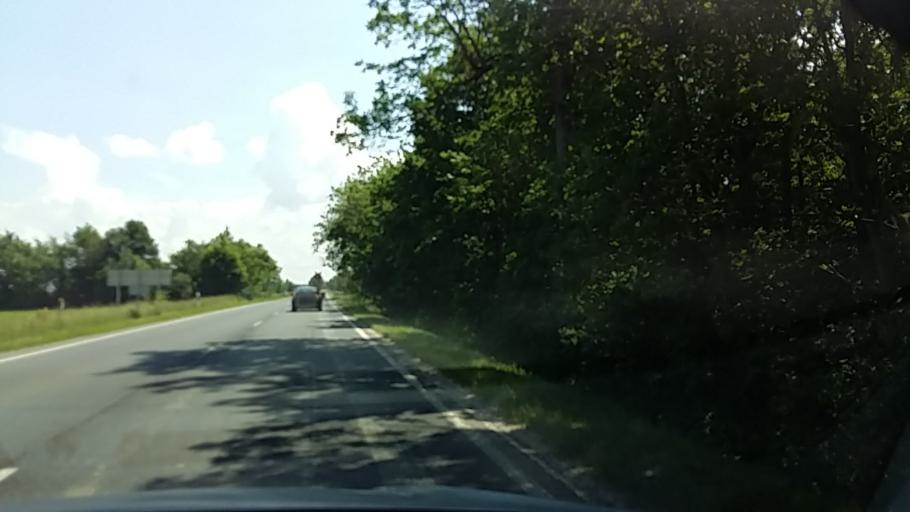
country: AT
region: Burgenland
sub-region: Politischer Bezirk Gussing
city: Heiligenbrunn
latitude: 46.9671
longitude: 16.4435
